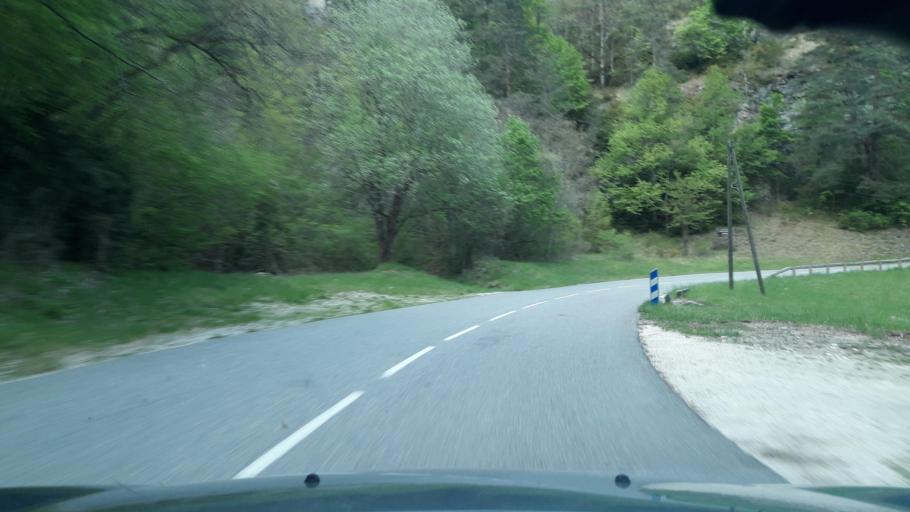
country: FR
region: Rhone-Alpes
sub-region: Departement de la Drome
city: Die
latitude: 44.6767
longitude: 5.5618
